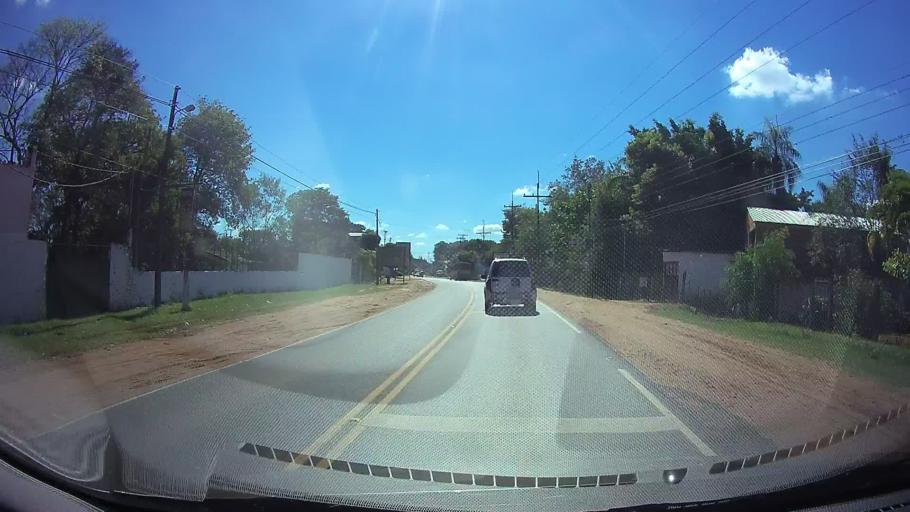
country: PY
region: Central
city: Limpio
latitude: -25.1920
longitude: -57.4634
